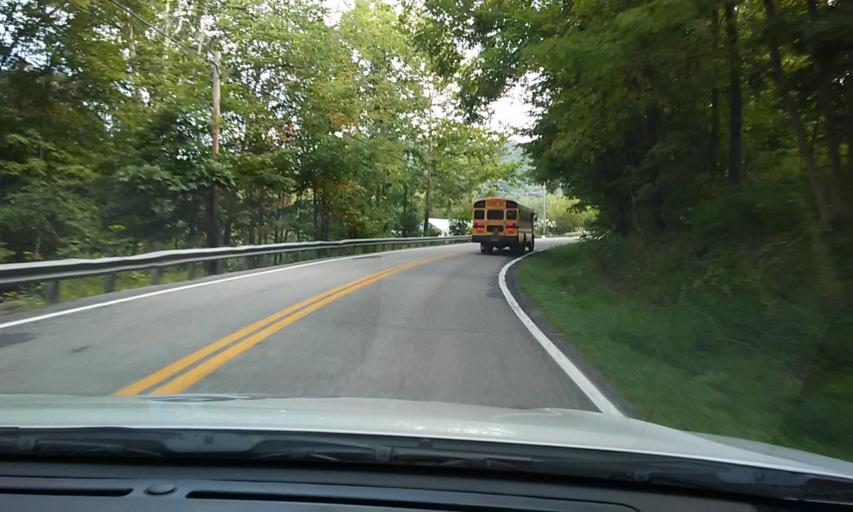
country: US
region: West Virginia
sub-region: Monongalia County
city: Star City
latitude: 39.7139
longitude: -80.1231
